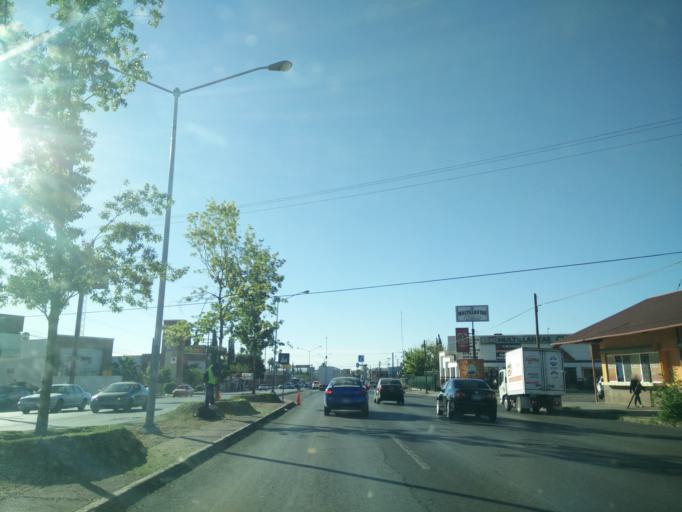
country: MX
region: Chihuahua
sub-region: Chihuahua
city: Chihuahua
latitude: 28.6700
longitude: -106.0951
